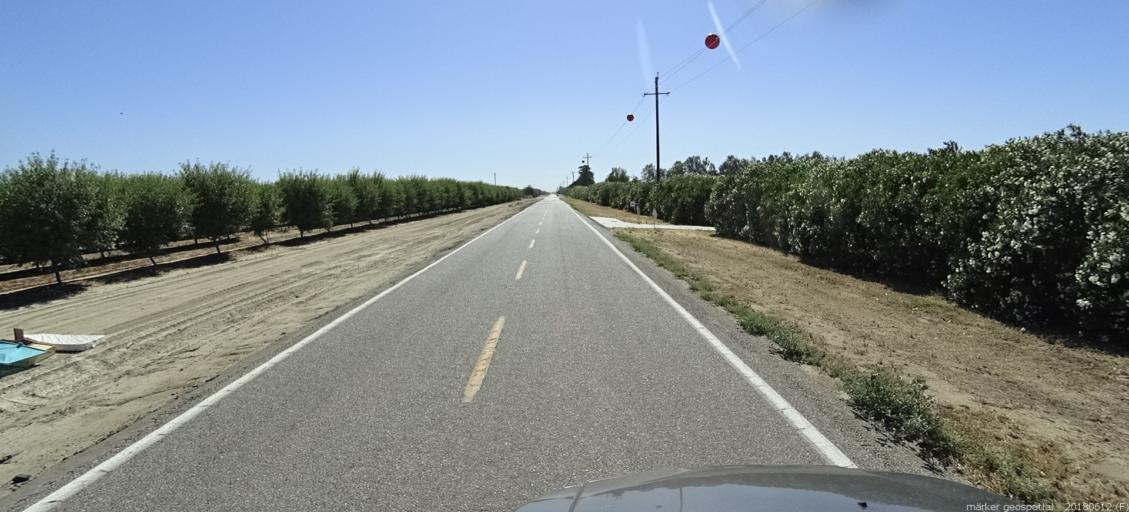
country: US
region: California
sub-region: Fresno County
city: Firebaugh
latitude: 37.0181
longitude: -120.4141
